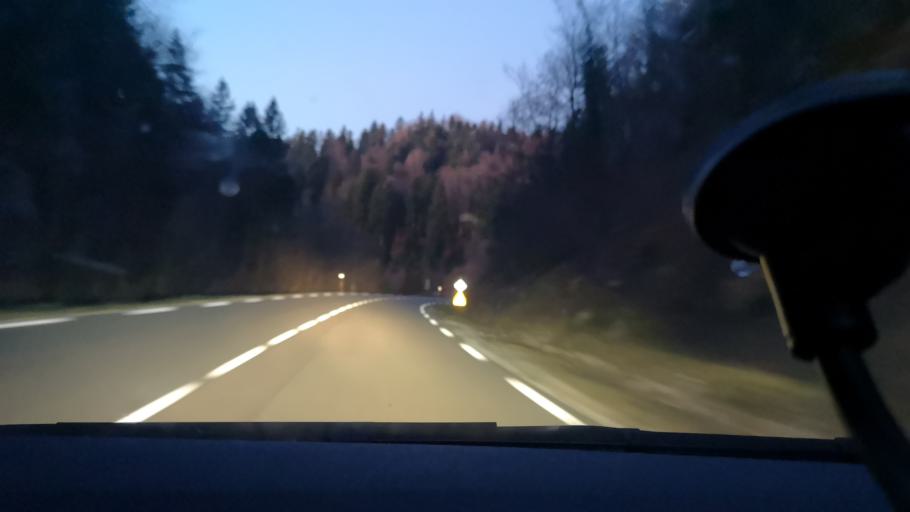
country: FR
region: Franche-Comte
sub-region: Departement du Jura
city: Champagnole
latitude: 46.7554
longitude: 5.9672
